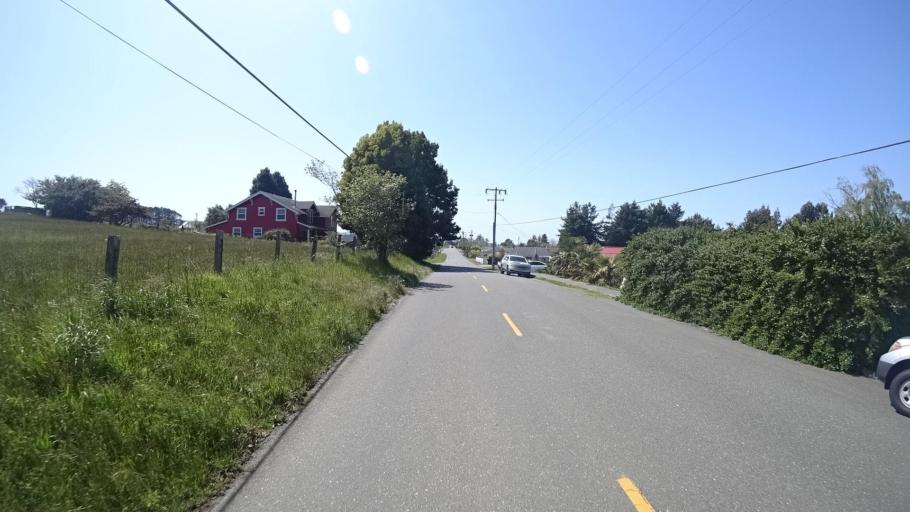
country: US
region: California
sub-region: Humboldt County
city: Hydesville
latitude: 40.5629
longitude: -124.1288
